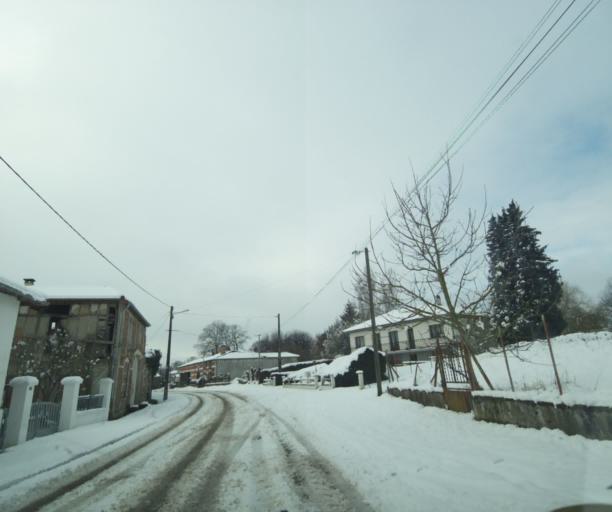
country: FR
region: Champagne-Ardenne
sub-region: Departement de la Haute-Marne
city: Montier-en-Der
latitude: 48.5144
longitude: 4.6975
